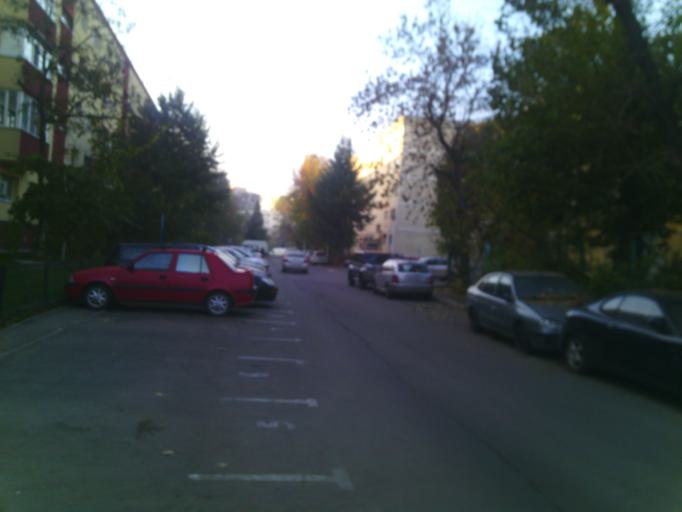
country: RO
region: Bucuresti
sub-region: Municipiul Bucuresti
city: Bucuresti
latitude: 44.3800
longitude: 26.0960
